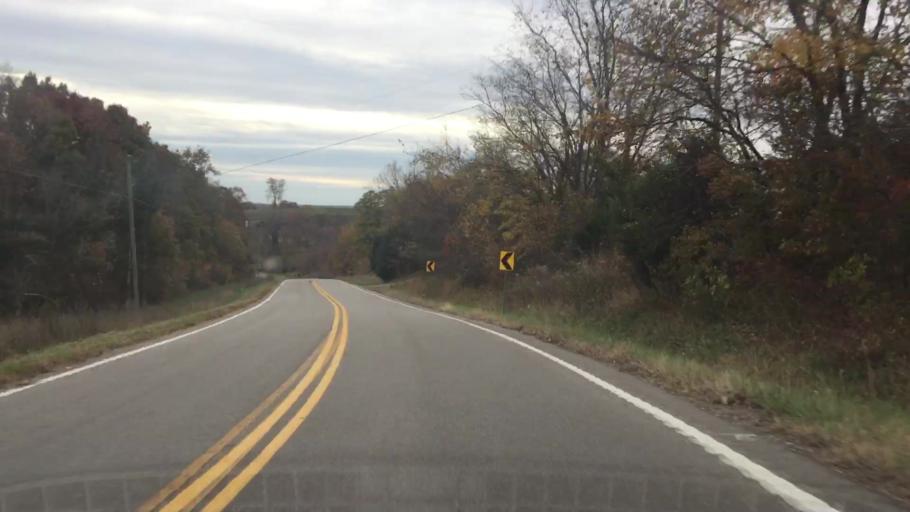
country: US
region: Missouri
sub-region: Callaway County
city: Fulton
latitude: 38.7125
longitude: -91.7377
